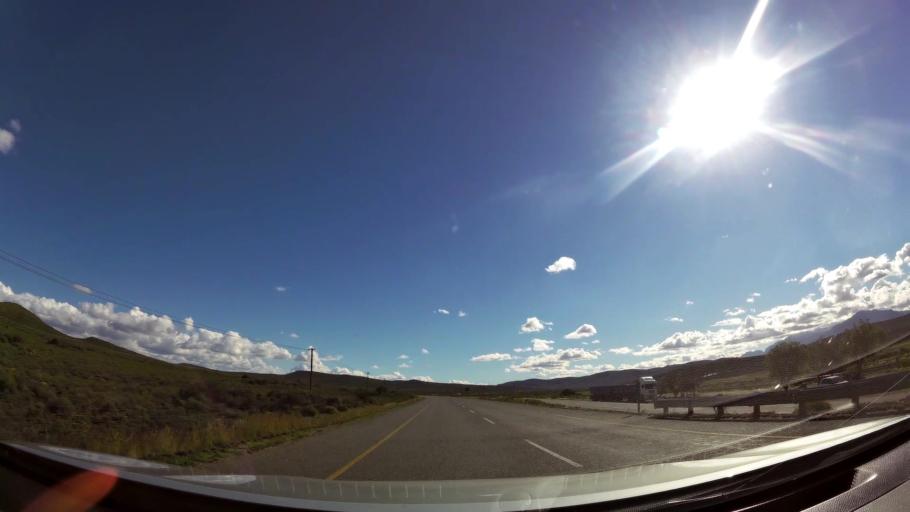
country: ZA
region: Western Cape
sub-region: Cape Winelands District Municipality
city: Worcester
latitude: -33.7512
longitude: 19.7180
